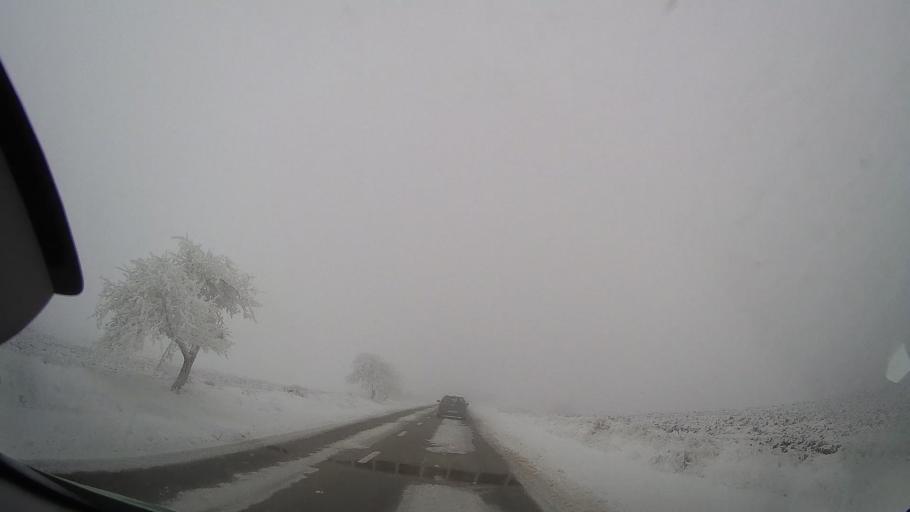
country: RO
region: Neamt
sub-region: Comuna Valea Ursului
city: Valea Ursului
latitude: 46.8269
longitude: 27.0623
